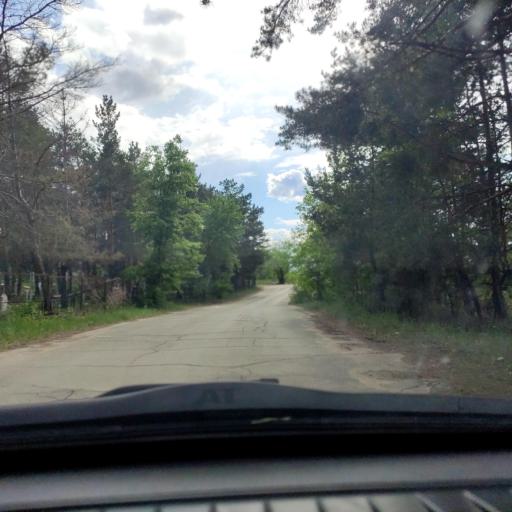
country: RU
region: Samara
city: Zhigulevsk
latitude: 53.5229
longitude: 49.5377
